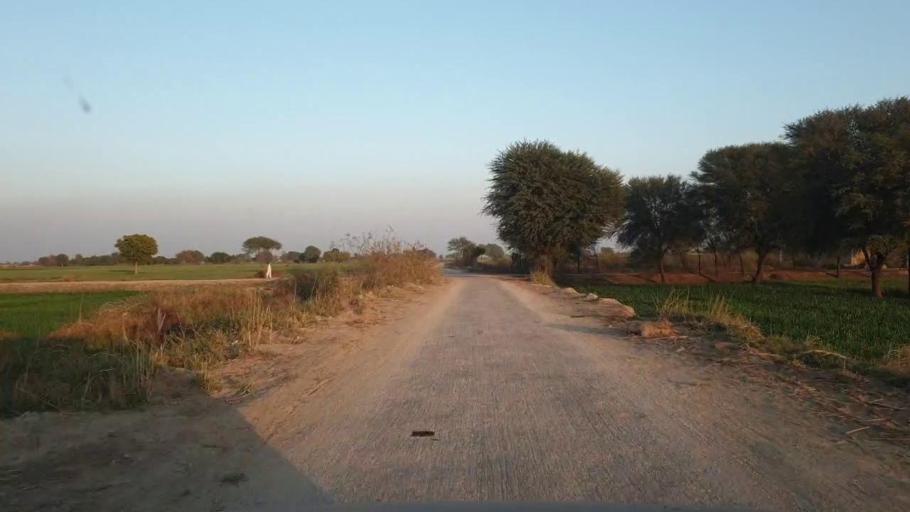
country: PK
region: Sindh
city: Tando Jam
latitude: 25.3012
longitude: 68.6444
